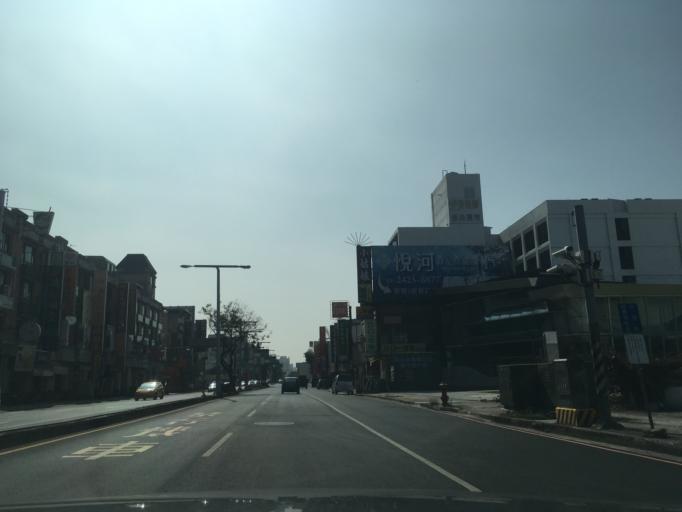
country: TW
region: Taiwan
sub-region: Taichung City
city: Taichung
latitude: 24.1967
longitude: 120.6574
